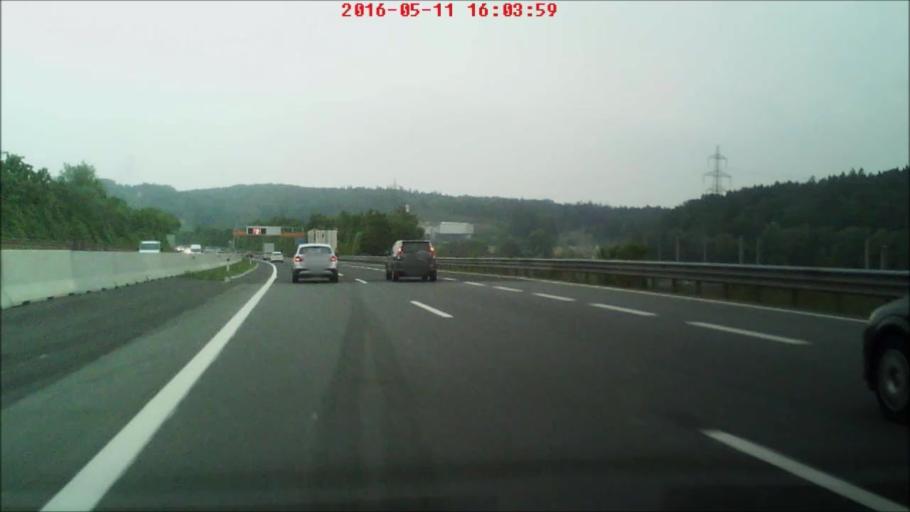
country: AT
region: Styria
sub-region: Politischer Bezirk Leibnitz
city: Weitendorf
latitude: 46.8918
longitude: 15.4718
